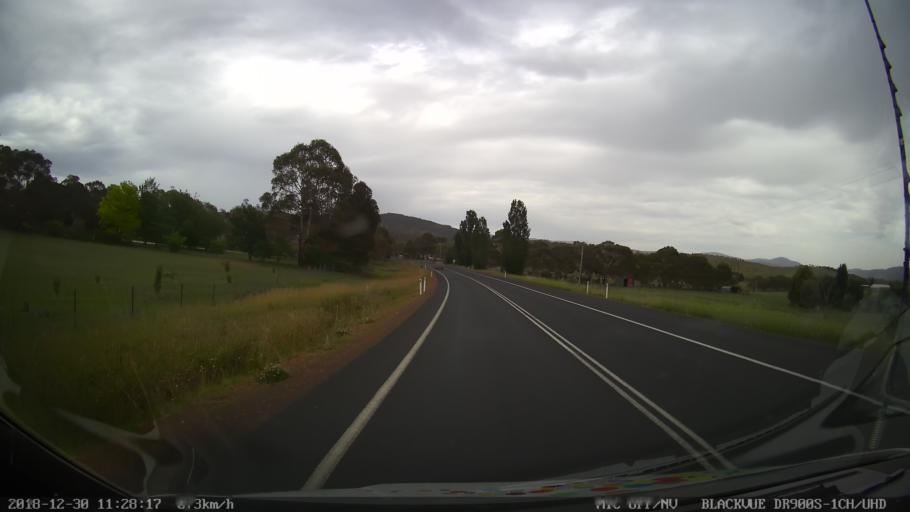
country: AU
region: New South Wales
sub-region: Snowy River
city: Jindabyne
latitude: -36.4537
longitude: 148.6196
